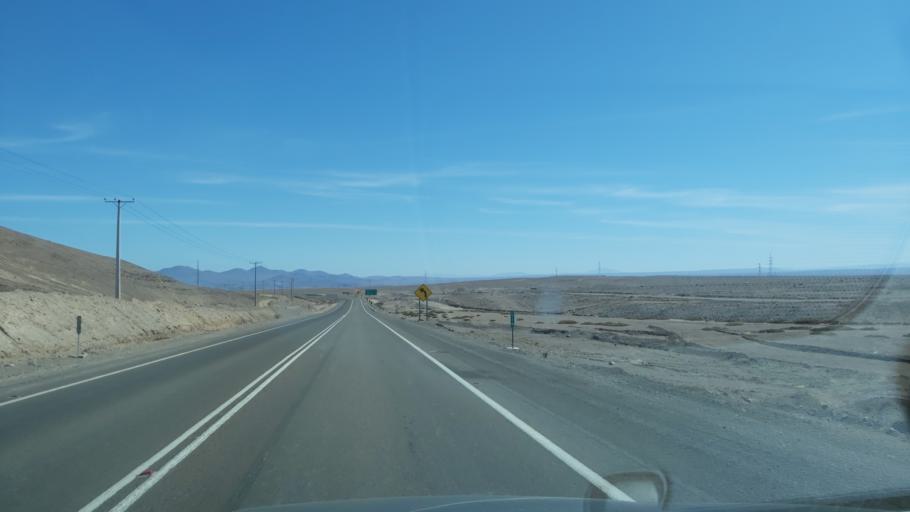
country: CL
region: Atacama
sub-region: Provincia de Chanaral
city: Diego de Almagro
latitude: -26.4564
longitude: -69.9858
